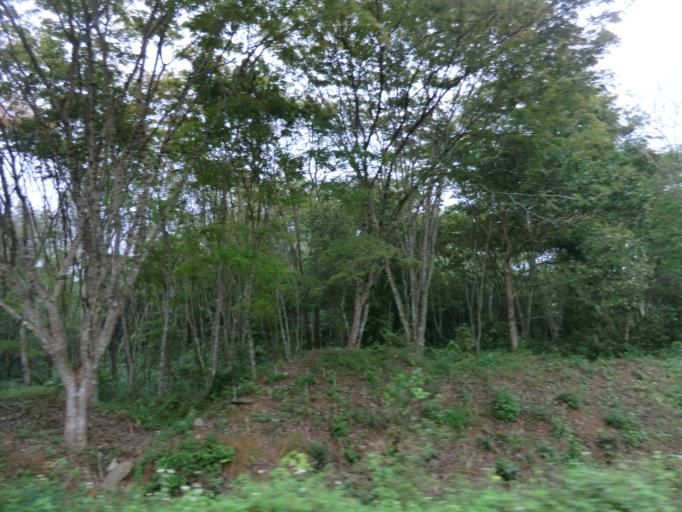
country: VN
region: Ninh Binh
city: Thi Tran Nho Quan
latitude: 20.2493
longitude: 105.7163
